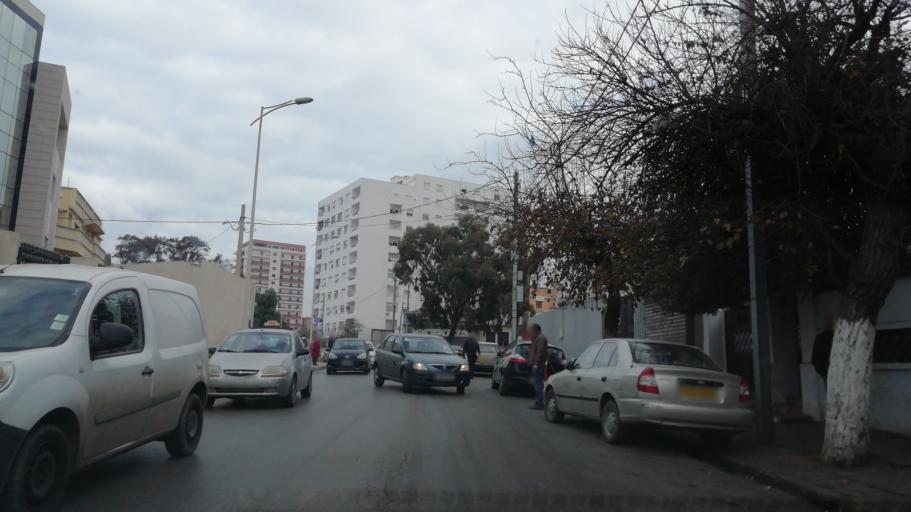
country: DZ
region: Oran
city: Oran
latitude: 35.7032
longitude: -0.6106
